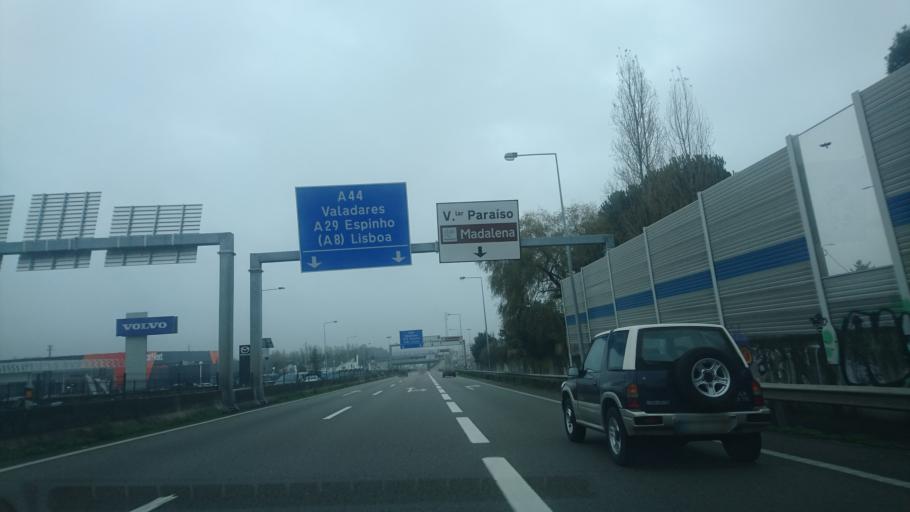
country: PT
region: Porto
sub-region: Vila Nova de Gaia
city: Vilar do Paraiso
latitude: 41.1121
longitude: -8.6266
